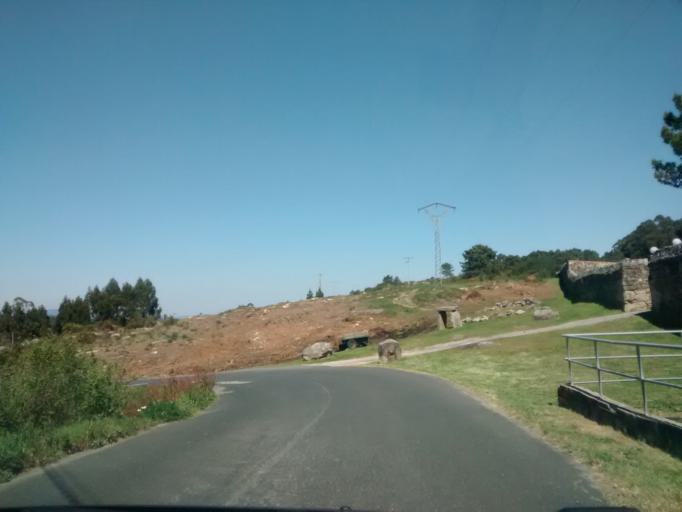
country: ES
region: Galicia
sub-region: Provincia de Pontevedra
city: O Grove
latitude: 42.4773
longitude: -8.8804
